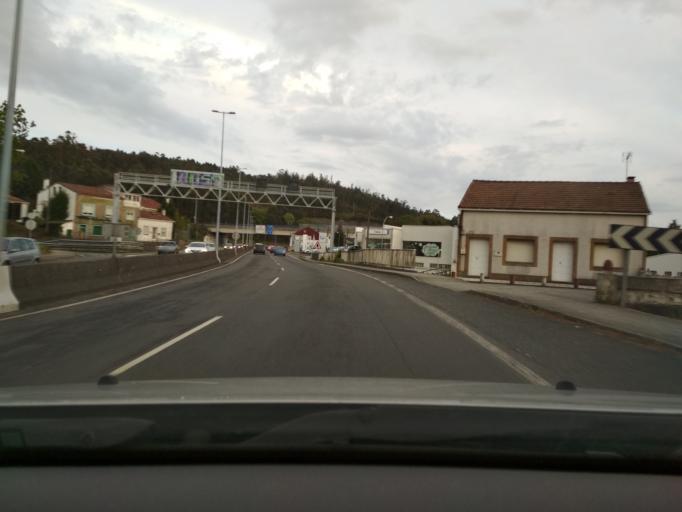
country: ES
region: Galicia
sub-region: Provincia da Coruna
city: Santiago de Compostela
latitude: 42.8585
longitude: -8.5720
